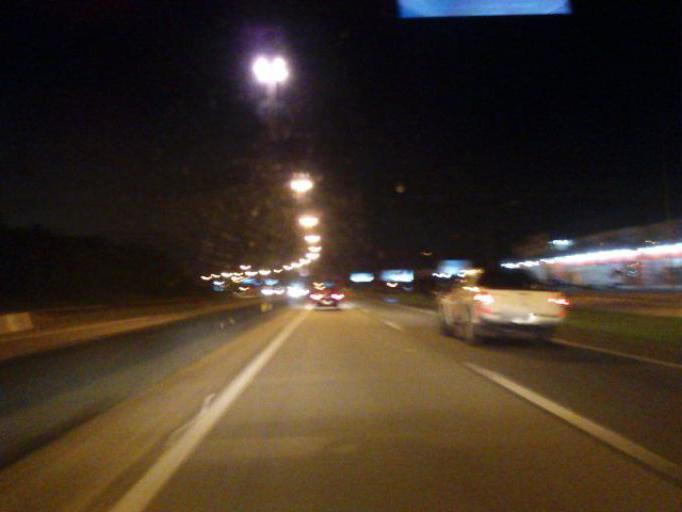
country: BR
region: Santa Catarina
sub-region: Balneario Camboriu
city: Balneario Camboriu
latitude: -26.9942
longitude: -48.6594
